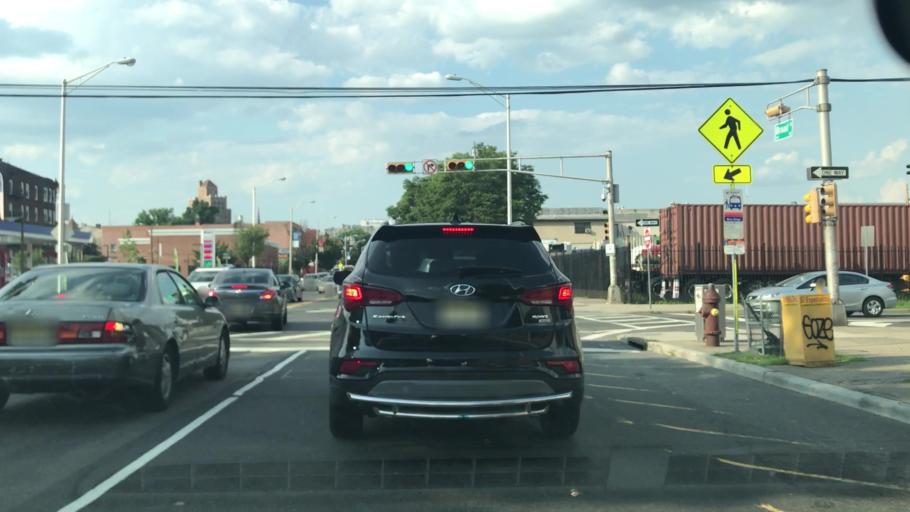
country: US
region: New Jersey
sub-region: Essex County
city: Newark
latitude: 40.7217
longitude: -74.1803
